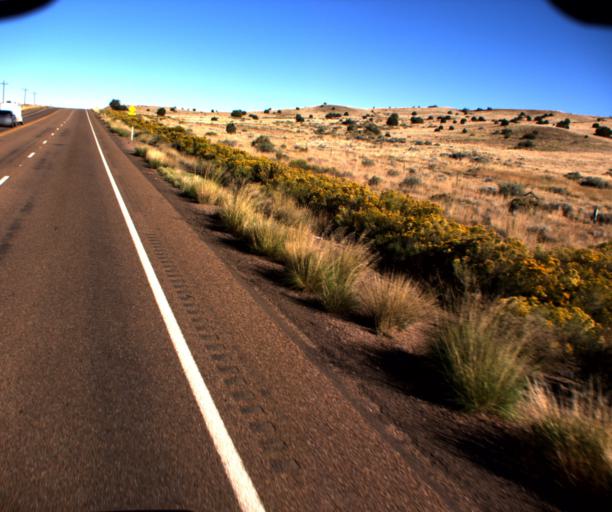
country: US
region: Arizona
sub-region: Navajo County
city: Taylor
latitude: 34.4268
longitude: -110.0899
